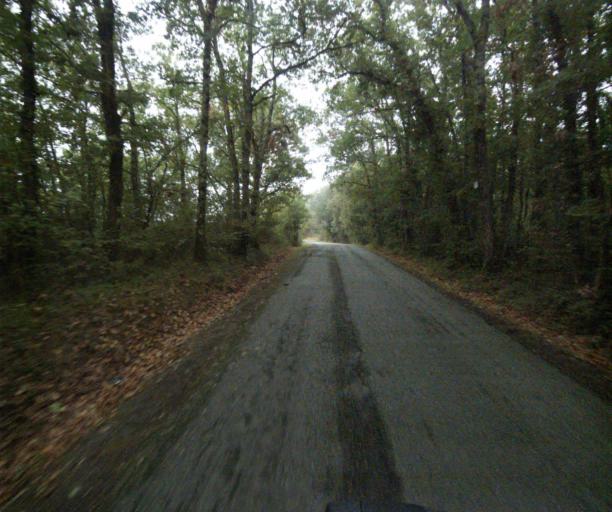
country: FR
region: Midi-Pyrenees
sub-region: Departement du Tarn-et-Garonne
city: Orgueil
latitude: 43.9291
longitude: 1.4307
